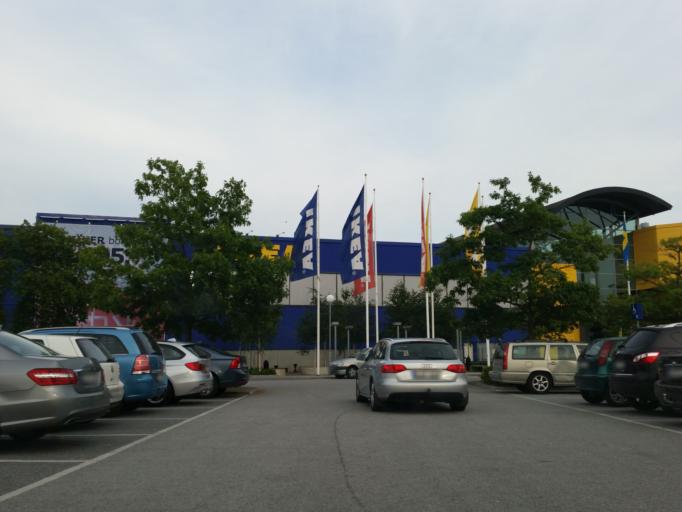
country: SE
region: Stockholm
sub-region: Jarfalla Kommun
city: Jakobsberg
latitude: 59.4210
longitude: 17.8570
